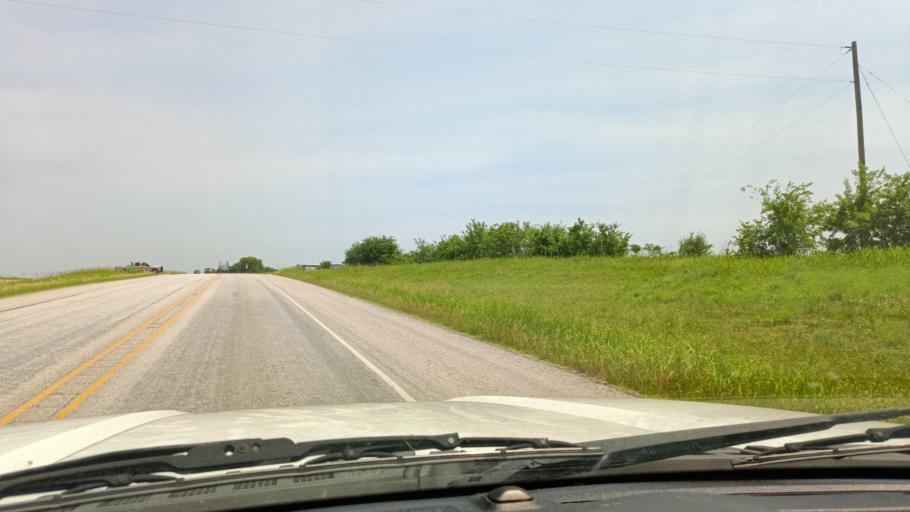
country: US
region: Texas
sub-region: Bell County
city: Rogers
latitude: 30.9531
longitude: -97.2550
